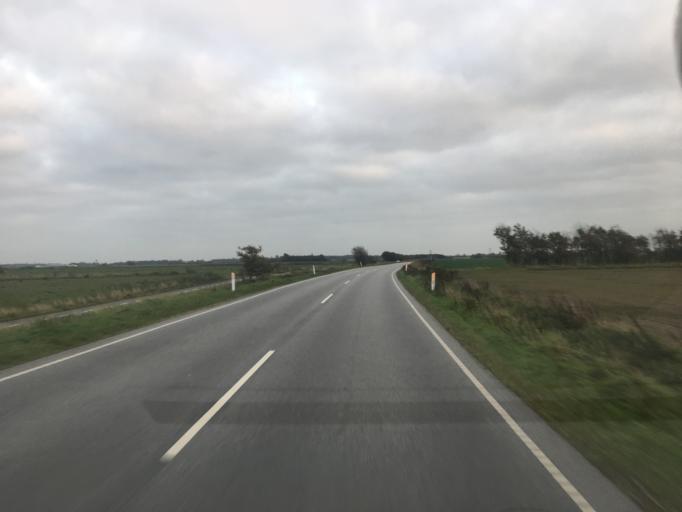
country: DE
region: Schleswig-Holstein
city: Aventoft
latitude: 54.9610
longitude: 8.7595
